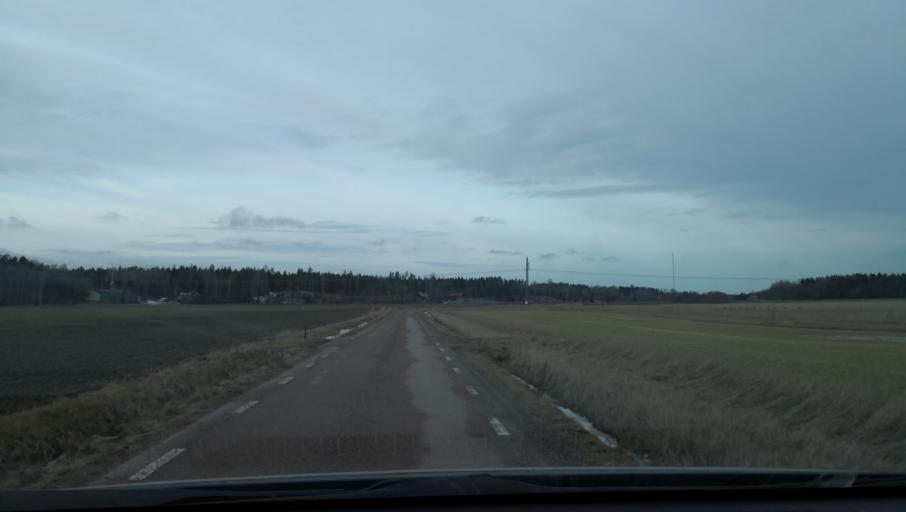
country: SE
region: Vaestmanland
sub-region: Vasteras
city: Skultuna
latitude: 59.5982
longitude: 16.4147
